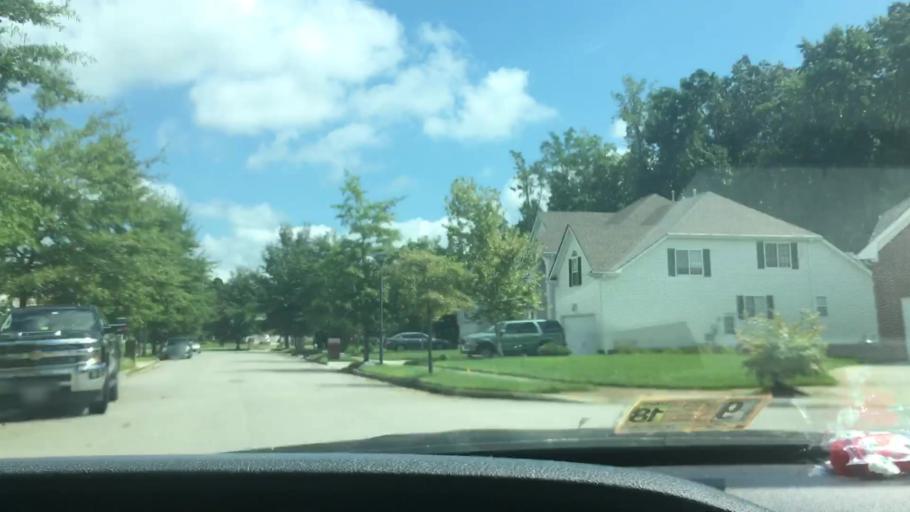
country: US
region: Virginia
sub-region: City of Virginia Beach
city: Virginia Beach
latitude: 36.7260
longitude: -76.0818
